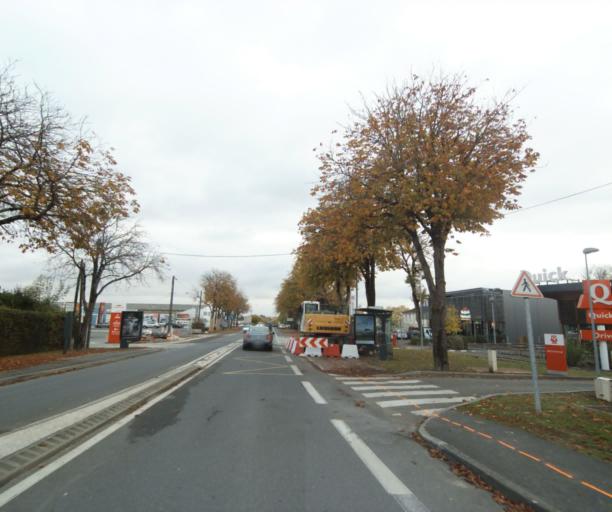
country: FR
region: Poitou-Charentes
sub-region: Departement de la Charente-Maritime
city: Saintes
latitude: 45.7544
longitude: -0.6554
